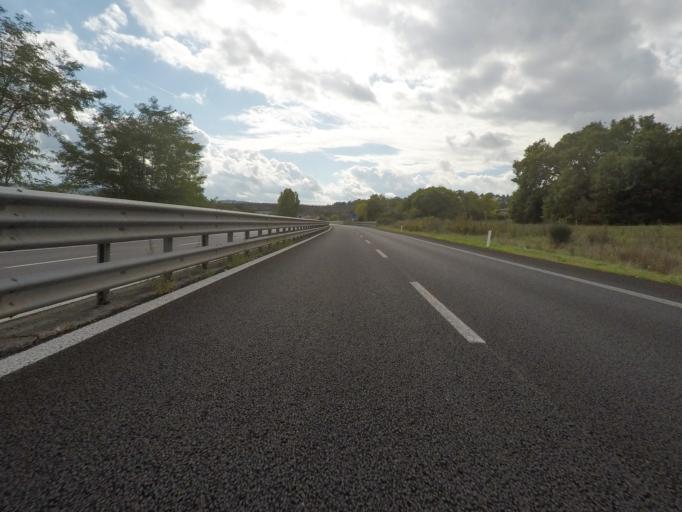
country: IT
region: Tuscany
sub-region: Provincia di Siena
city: Serre di Rapolano
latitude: 43.2589
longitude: 11.6319
